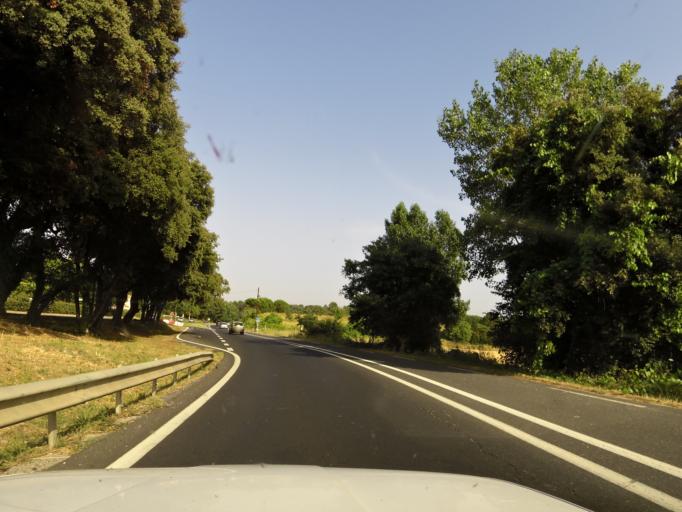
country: FR
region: Languedoc-Roussillon
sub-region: Departement de l'Herault
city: Clapiers
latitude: 43.6478
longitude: 3.8852
